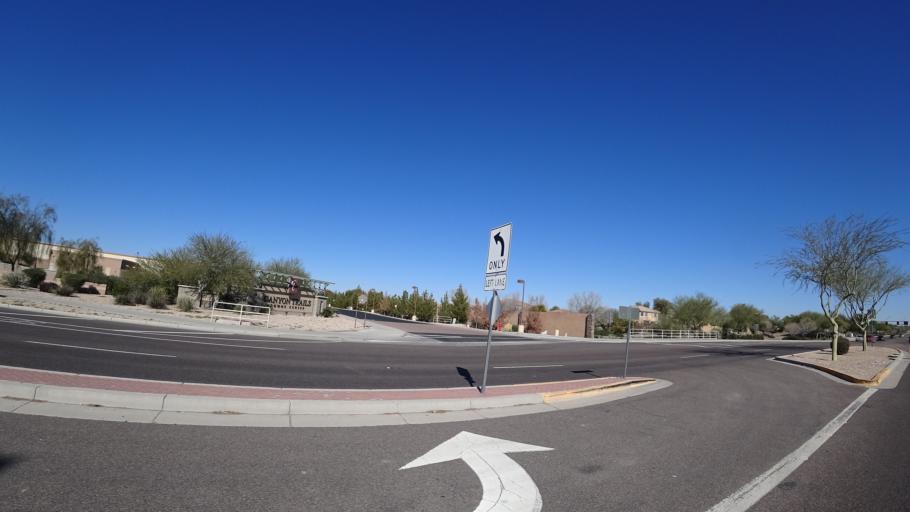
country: US
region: Arizona
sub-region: Maricopa County
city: Goodyear
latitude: 33.4356
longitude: -112.4207
